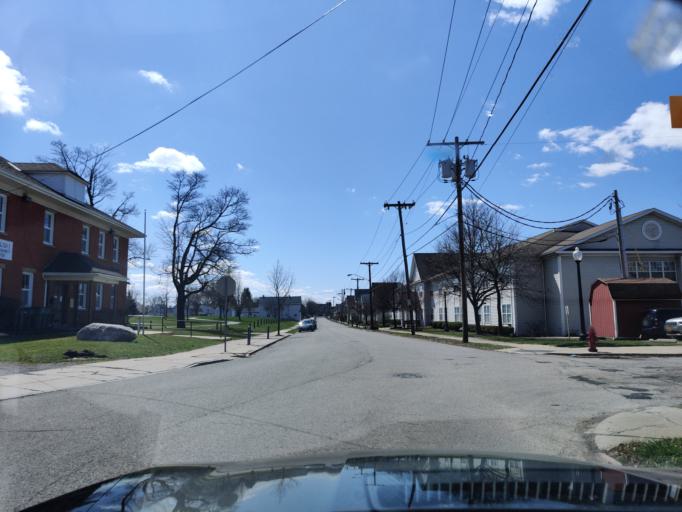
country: US
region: New York
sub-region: Erie County
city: Sloan
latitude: 42.8813
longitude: -78.8325
